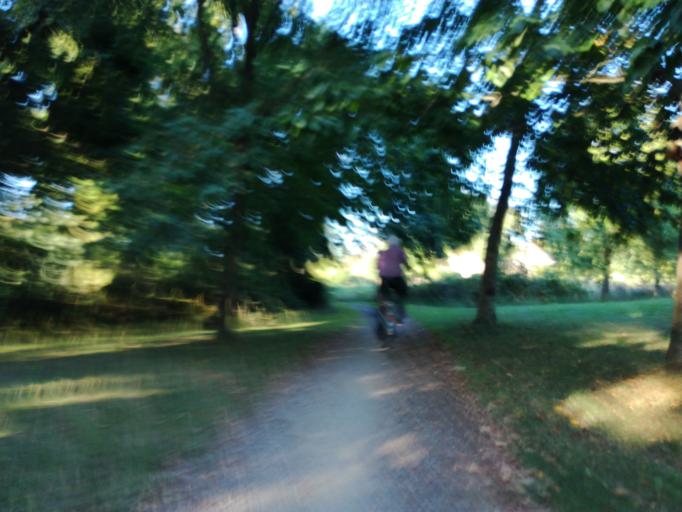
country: FR
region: Brittany
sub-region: Departement d'Ille-et-Vilaine
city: Betton
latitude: 48.1655
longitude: -1.6347
